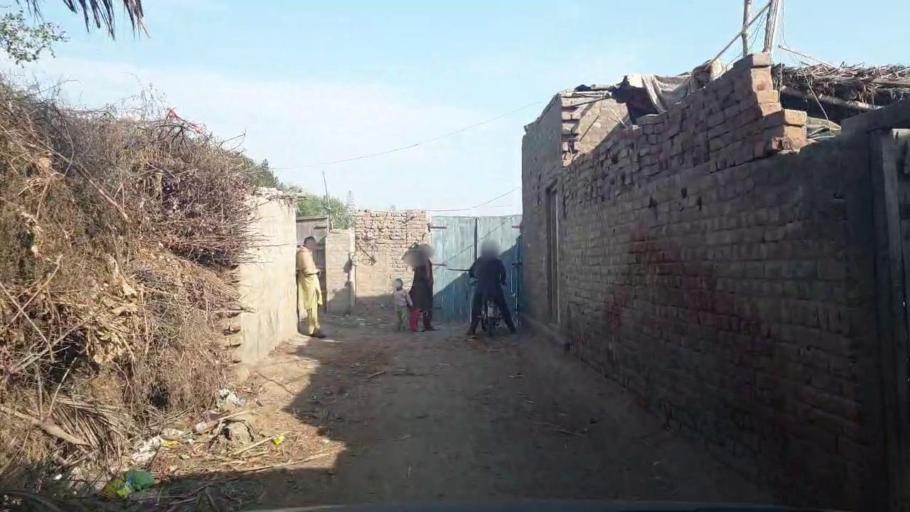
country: PK
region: Sindh
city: Tando Adam
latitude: 25.7550
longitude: 68.5970
